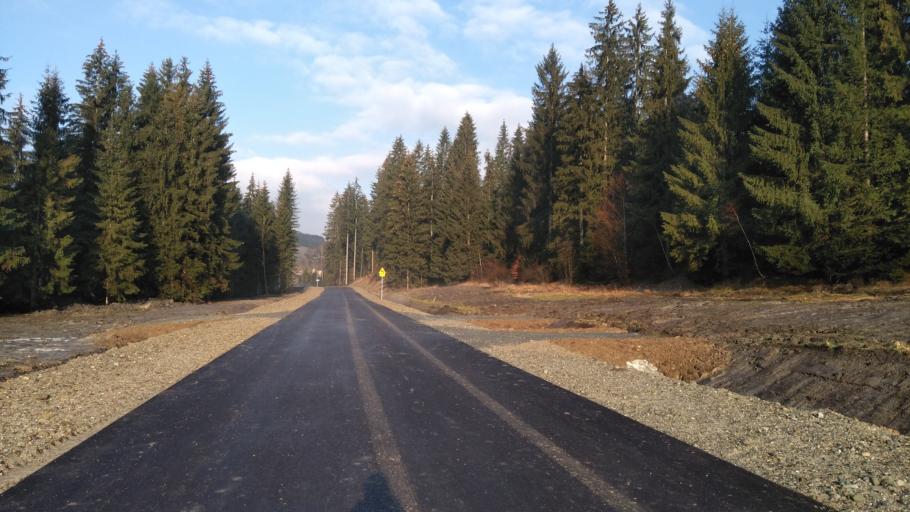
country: PL
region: Silesian Voivodeship
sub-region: Powiat cieszynski
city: Jaworzynka
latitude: 49.5169
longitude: 18.8767
